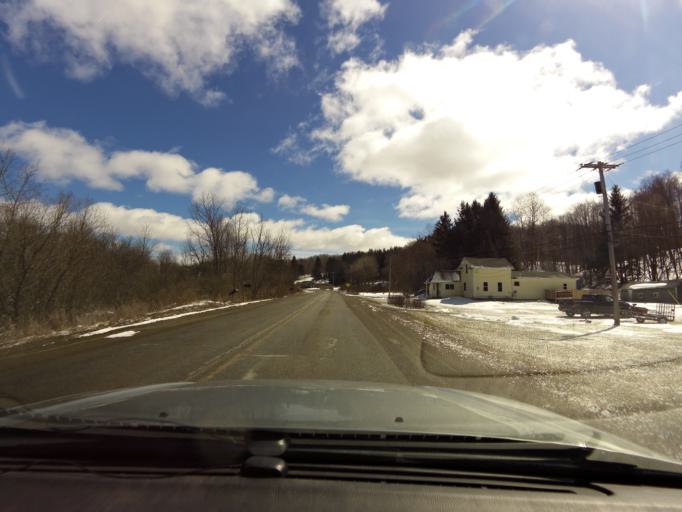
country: US
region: New York
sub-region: Cattaraugus County
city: Franklinville
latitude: 42.3436
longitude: -78.4428
